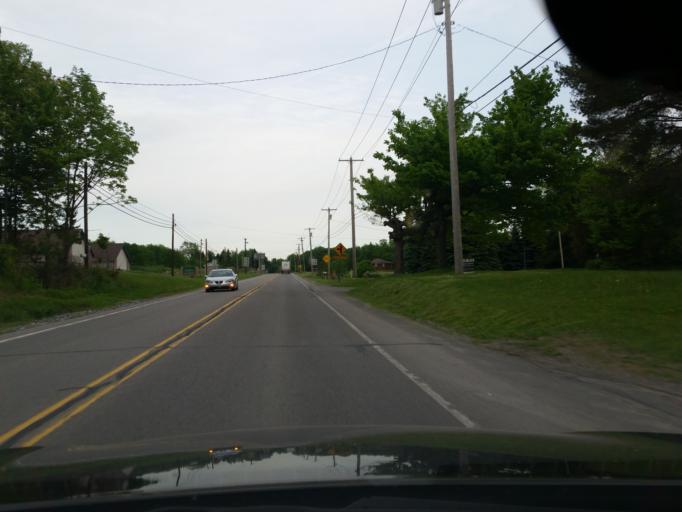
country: US
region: Pennsylvania
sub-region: Elk County
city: Ridgway
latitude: 41.4055
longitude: -78.7059
